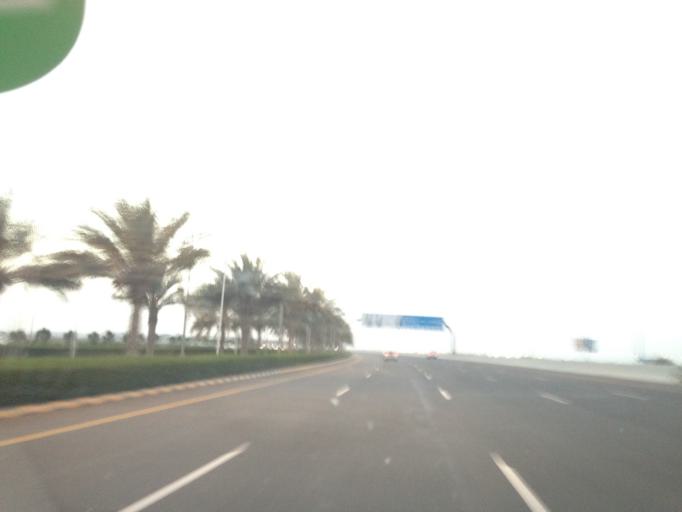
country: OM
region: Muhafazat Masqat
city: Bawshar
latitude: 23.6024
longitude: 58.3239
